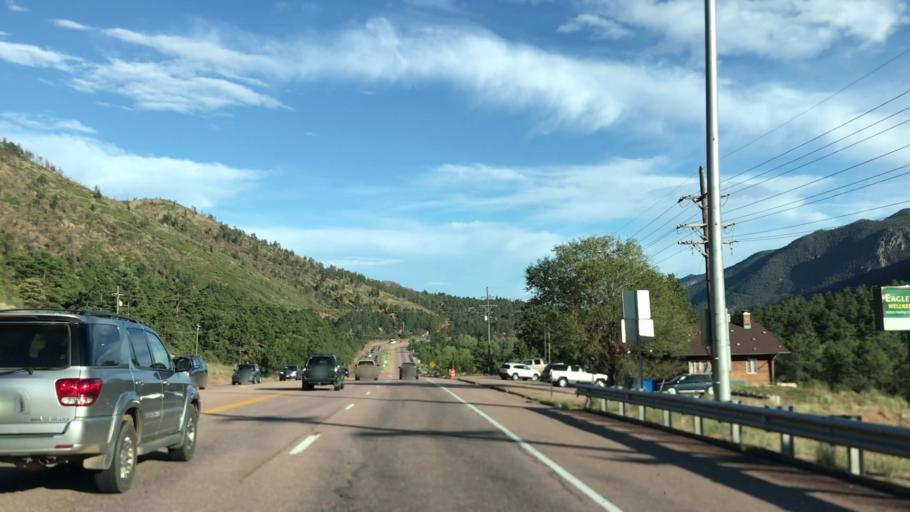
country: US
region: Colorado
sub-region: El Paso County
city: Cascade-Chipita Park
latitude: 38.9126
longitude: -104.9776
